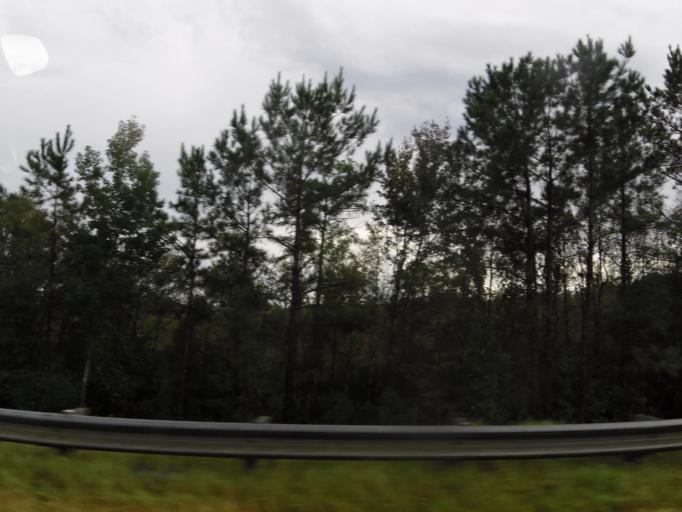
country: US
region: Georgia
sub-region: Long County
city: Ludowici
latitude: 31.6904
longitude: -81.7882
